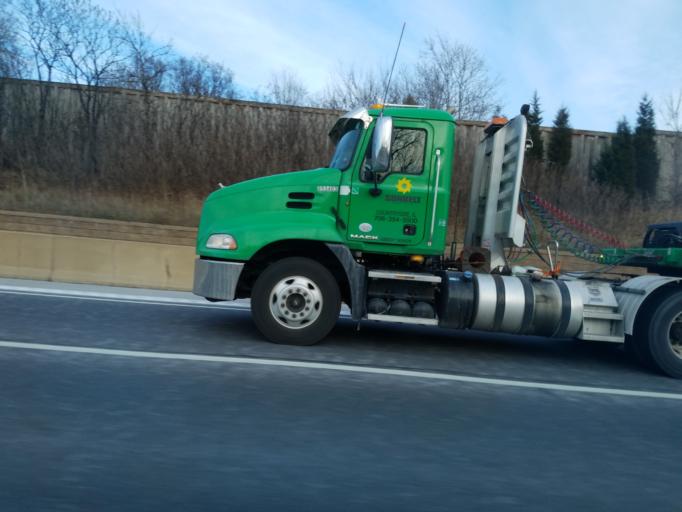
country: US
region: Illinois
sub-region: DuPage County
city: Woodridge
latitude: 41.7628
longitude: -88.0367
